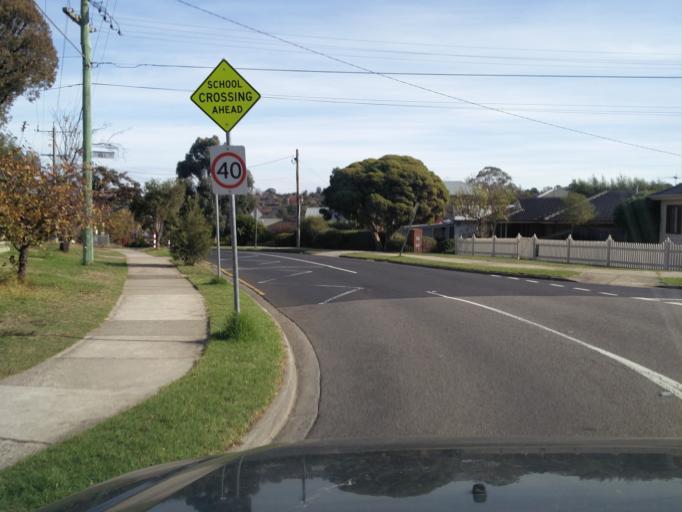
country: AU
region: Victoria
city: Macleod
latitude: -37.7331
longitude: 145.0743
